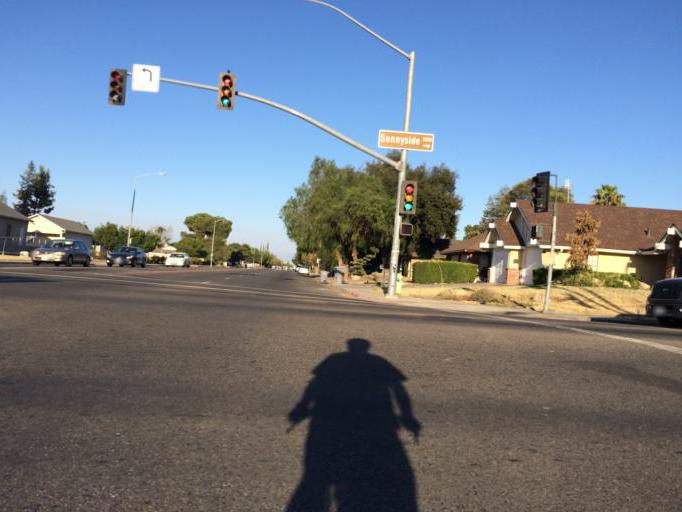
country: US
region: California
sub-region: Fresno County
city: Clovis
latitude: 36.8157
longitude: -119.6911
